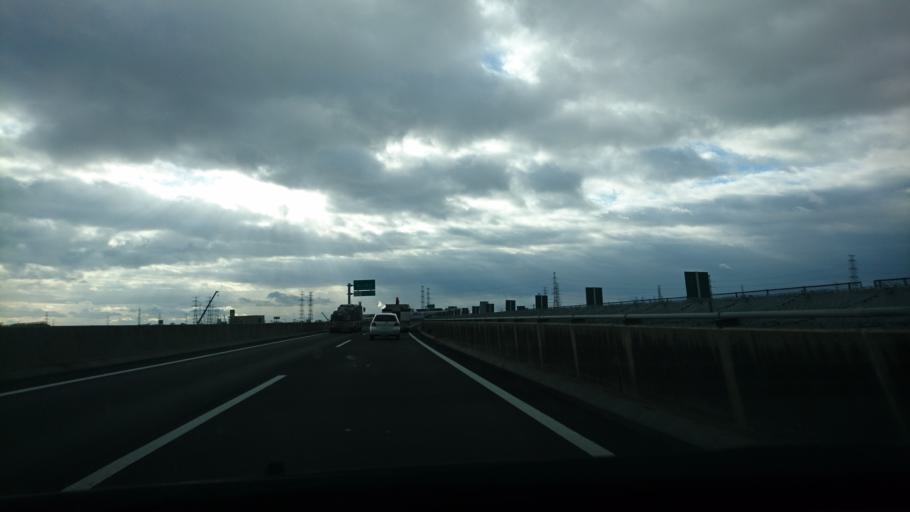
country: JP
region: Miyagi
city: Rifu
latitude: 38.2918
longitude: 140.9912
